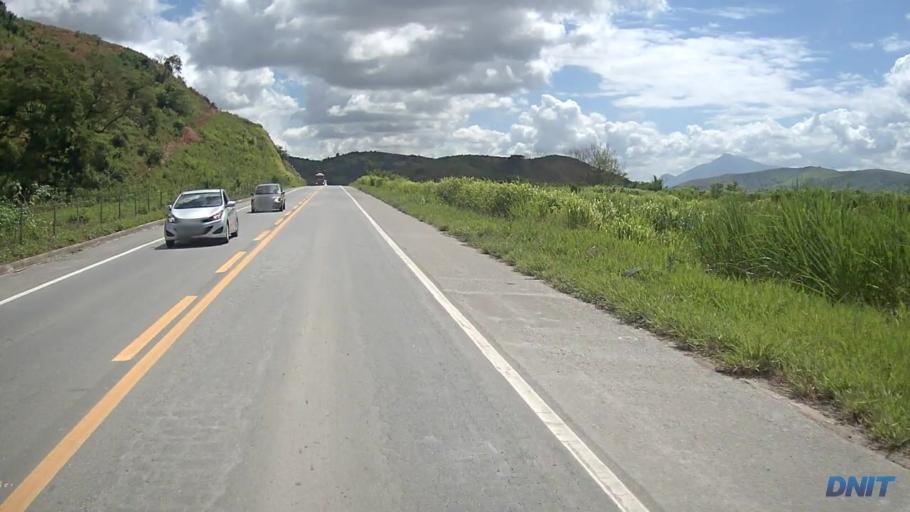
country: BR
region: Minas Gerais
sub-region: Governador Valadares
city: Governador Valadares
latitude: -18.9745
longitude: -42.0966
